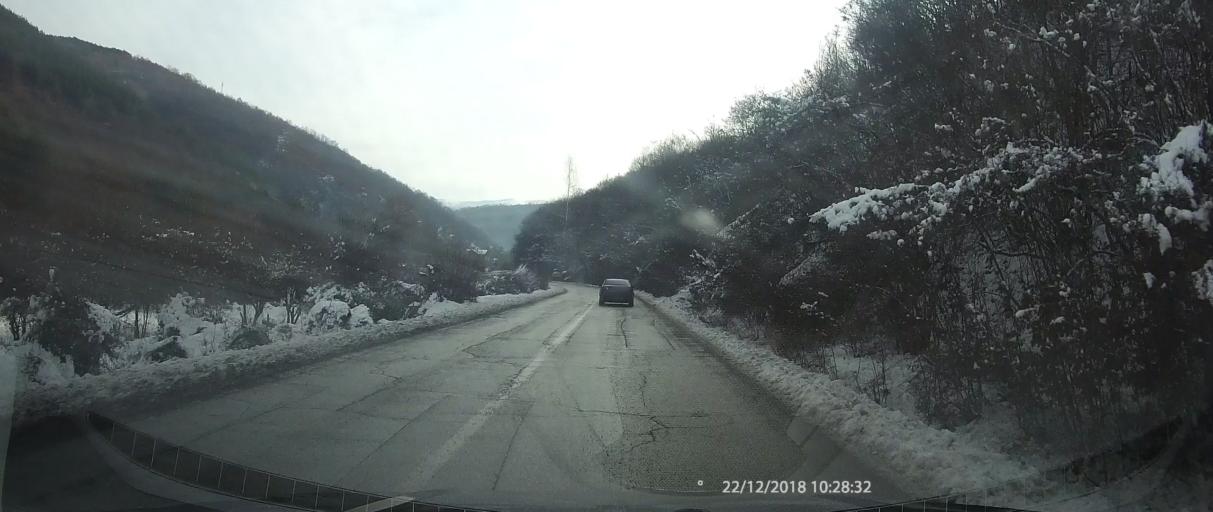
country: MK
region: Kriva Palanka
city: Kriva Palanka
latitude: 42.2269
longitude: 22.3842
